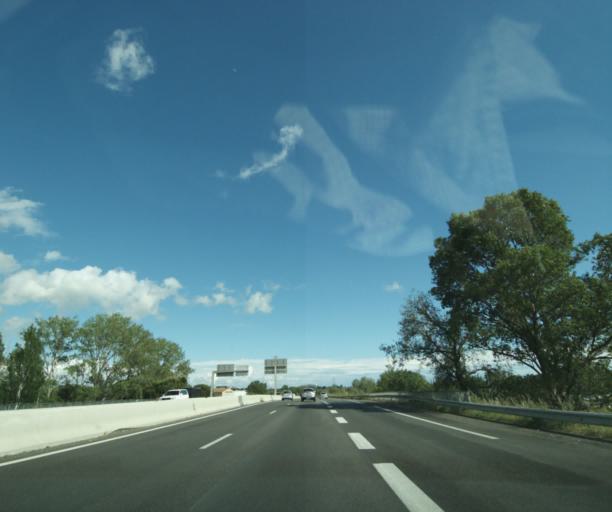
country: FR
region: Provence-Alpes-Cote d'Azur
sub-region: Departement des Bouches-du-Rhone
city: Arles
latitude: 43.6653
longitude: 4.6316
